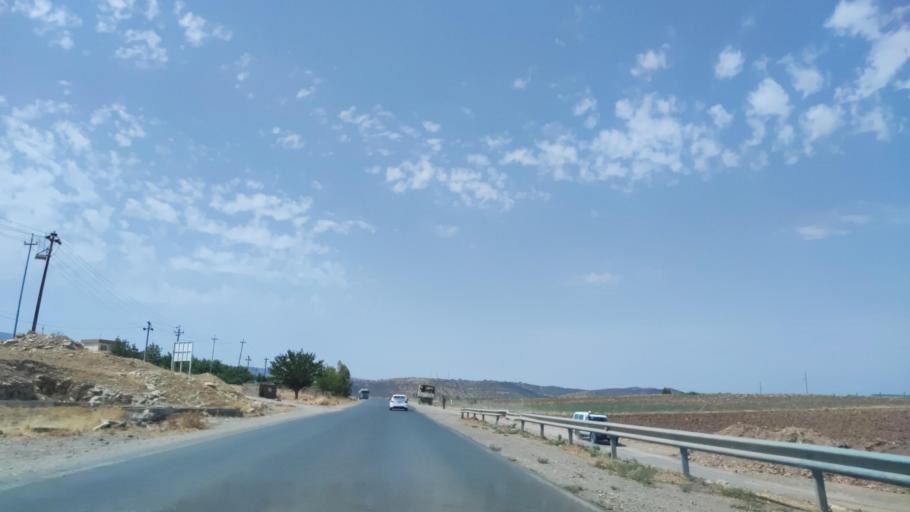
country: IQ
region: Arbil
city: Shaqlawah
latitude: 36.4641
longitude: 44.3932
